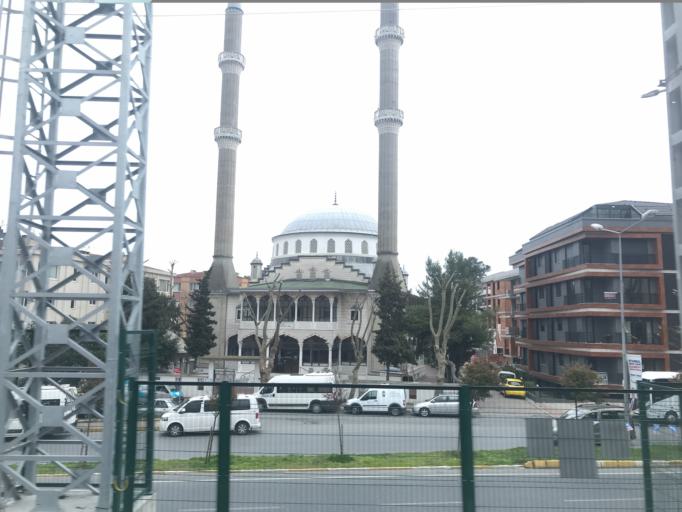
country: TR
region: Istanbul
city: Bahcelievler
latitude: 40.9662
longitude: 28.8384
